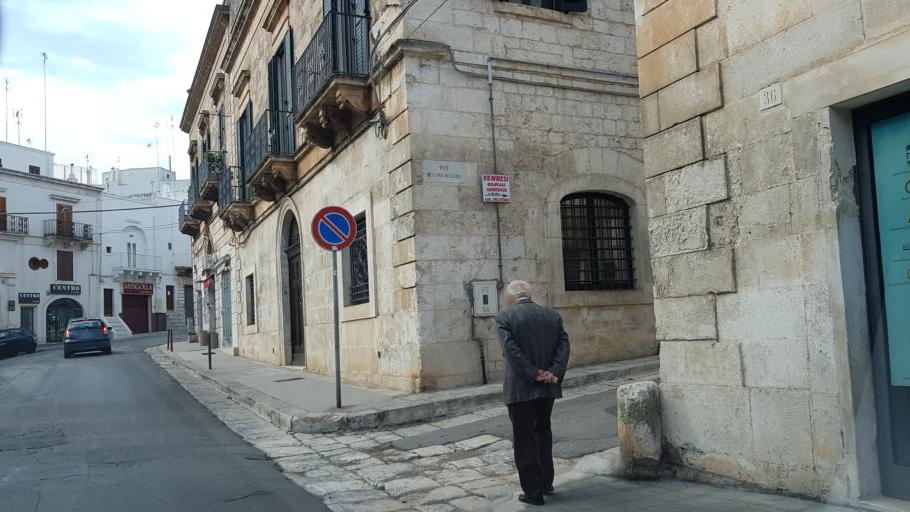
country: IT
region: Apulia
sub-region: Provincia di Brindisi
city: Ostuni
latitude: 40.7297
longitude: 17.5787
